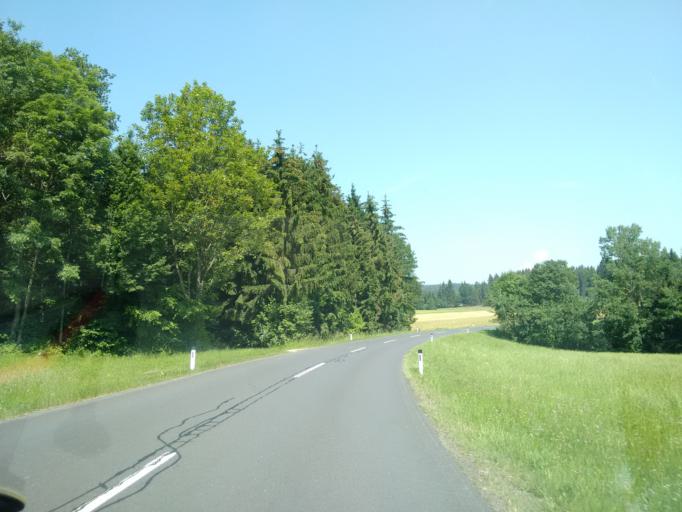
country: AT
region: Upper Austria
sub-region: Politischer Bezirk Urfahr-Umgebung
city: Altenberg bei Linz
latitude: 48.3996
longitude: 14.3428
